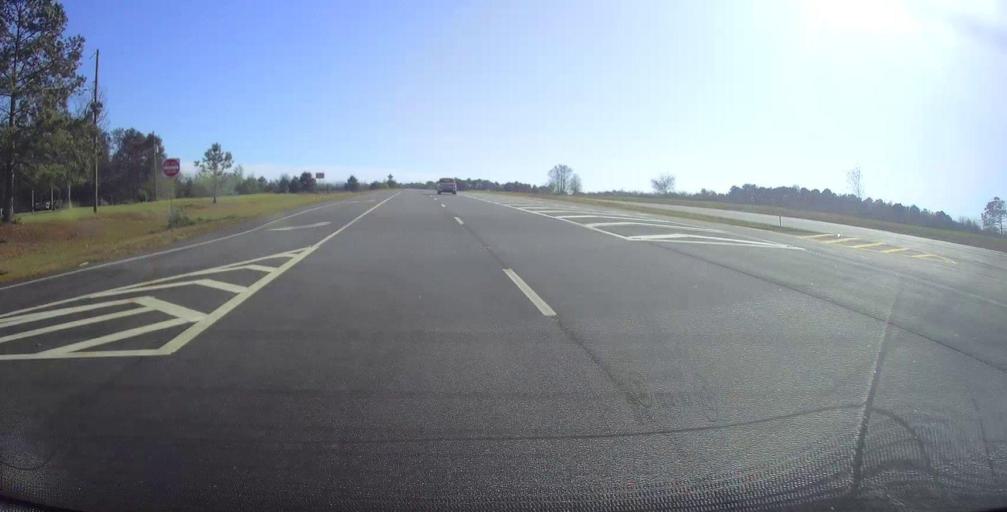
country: US
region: Georgia
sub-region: Peach County
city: Fort Valley
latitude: 32.5656
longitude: -83.9359
